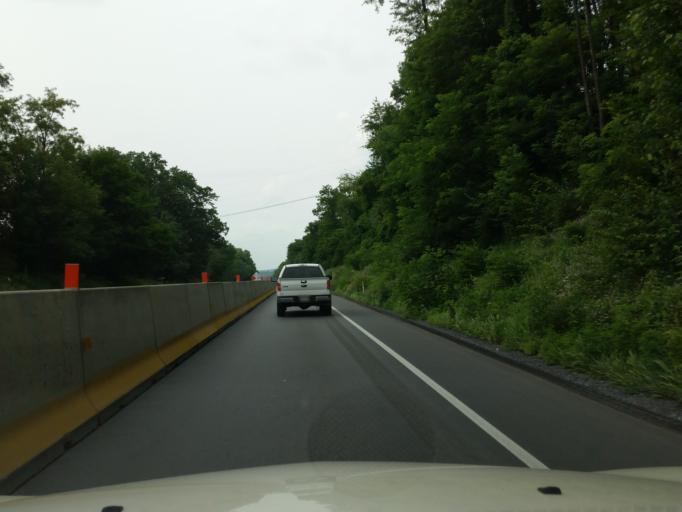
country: US
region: Pennsylvania
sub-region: Mifflin County
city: Lewistown
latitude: 40.5906
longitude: -77.5572
